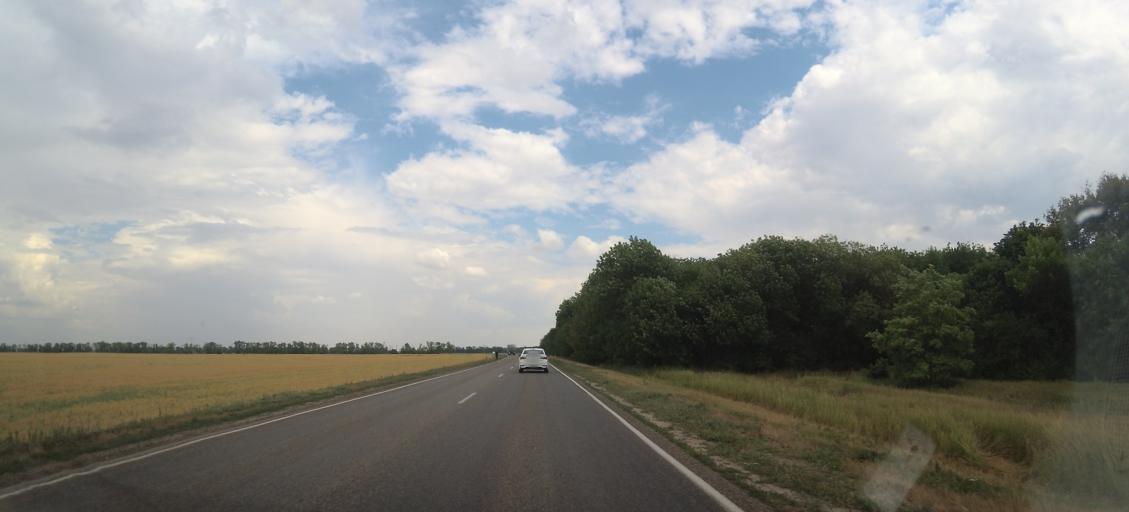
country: RU
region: Rostov
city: Peschanokopskoye
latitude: 46.2038
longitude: 41.2373
